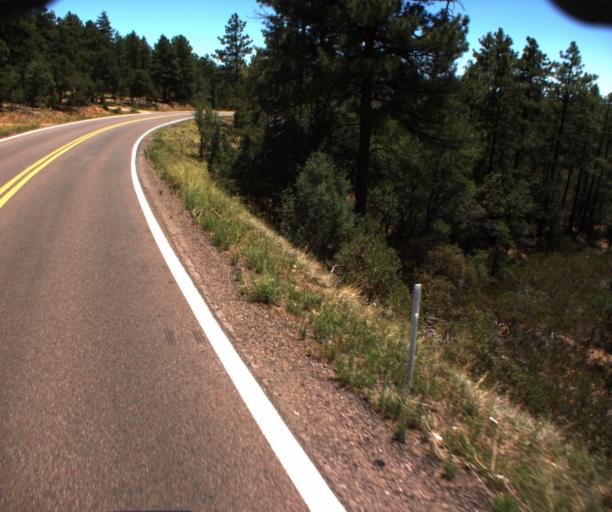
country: US
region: Arizona
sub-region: Gila County
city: Pine
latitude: 34.3989
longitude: -111.4705
